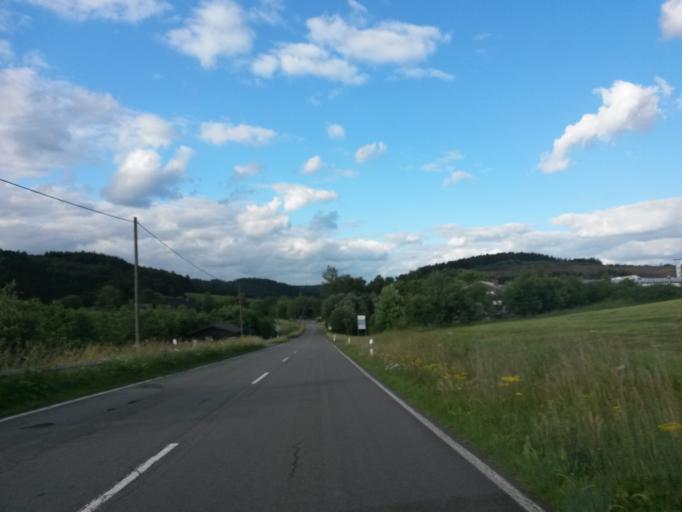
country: DE
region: North Rhine-Westphalia
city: Meinerzhagen
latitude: 51.0723
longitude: 7.7070
